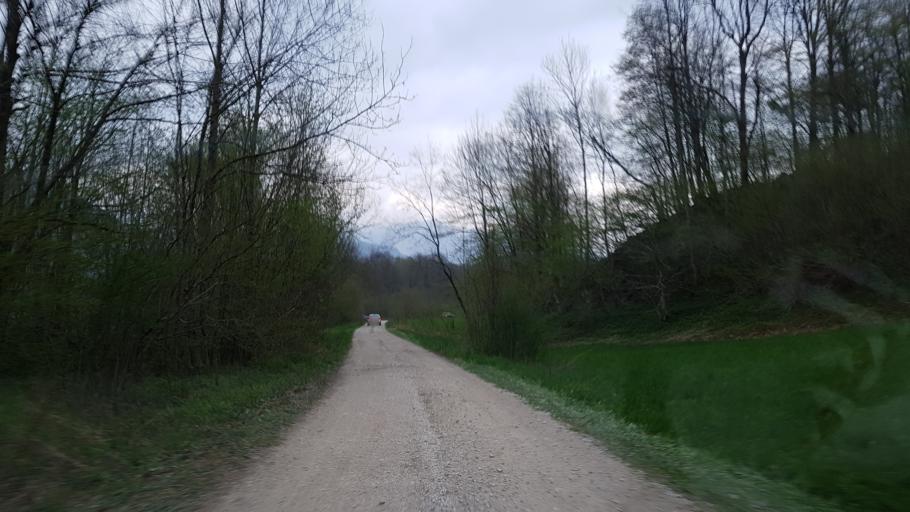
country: SI
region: Kobarid
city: Kobarid
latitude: 46.2404
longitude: 13.5396
